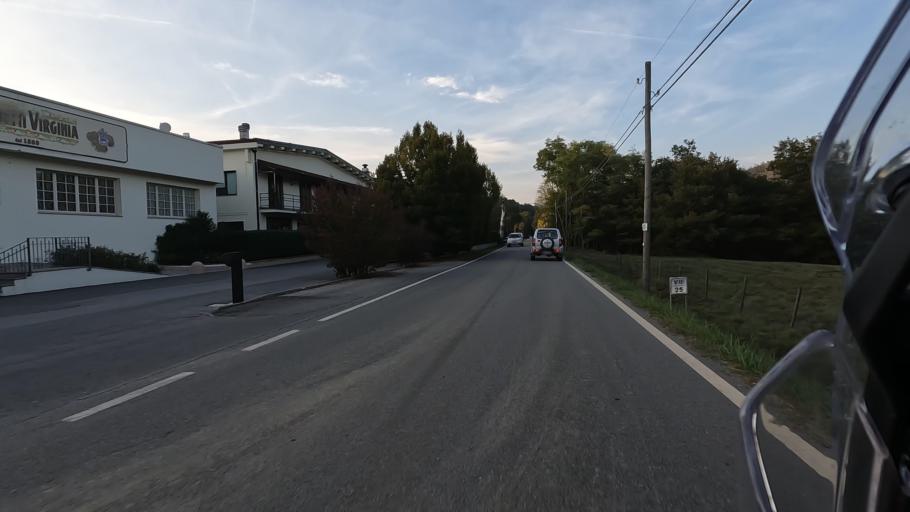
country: IT
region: Liguria
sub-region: Provincia di Savona
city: Sassello
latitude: 44.5026
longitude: 8.4843
